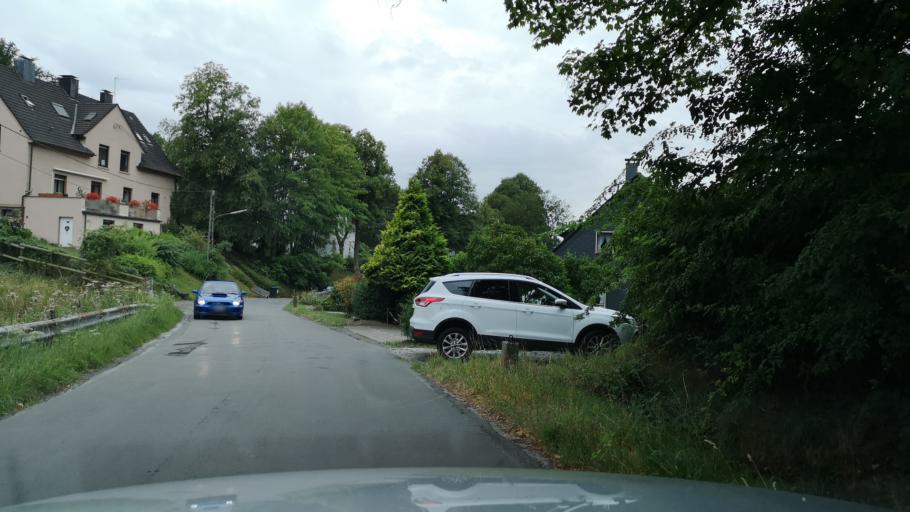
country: DE
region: North Rhine-Westphalia
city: Hattingen
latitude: 51.3872
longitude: 7.1195
